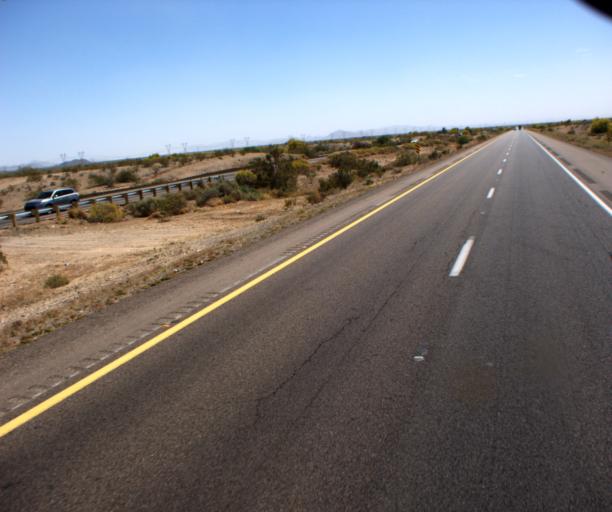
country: US
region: Arizona
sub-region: Maricopa County
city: Gila Bend
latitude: 33.0806
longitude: -112.6474
